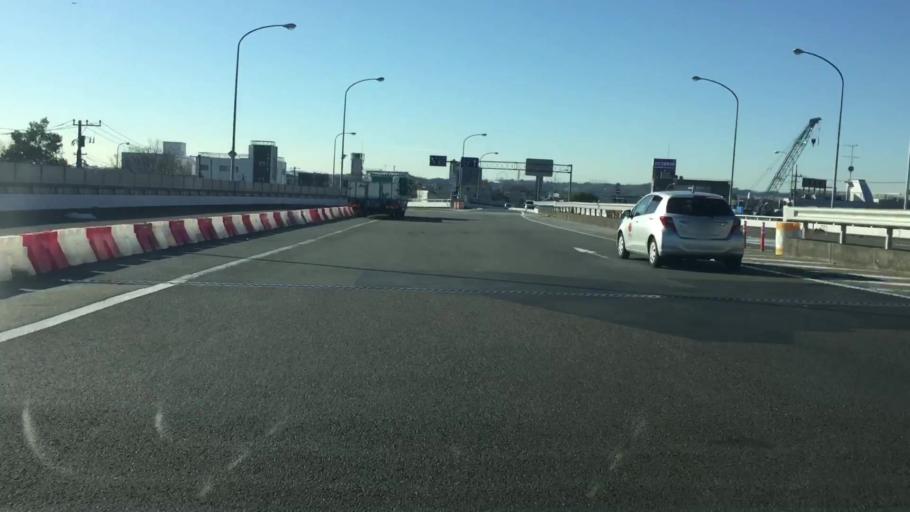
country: JP
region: Tokyo
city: Chofugaoka
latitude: 35.6598
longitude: 139.5357
